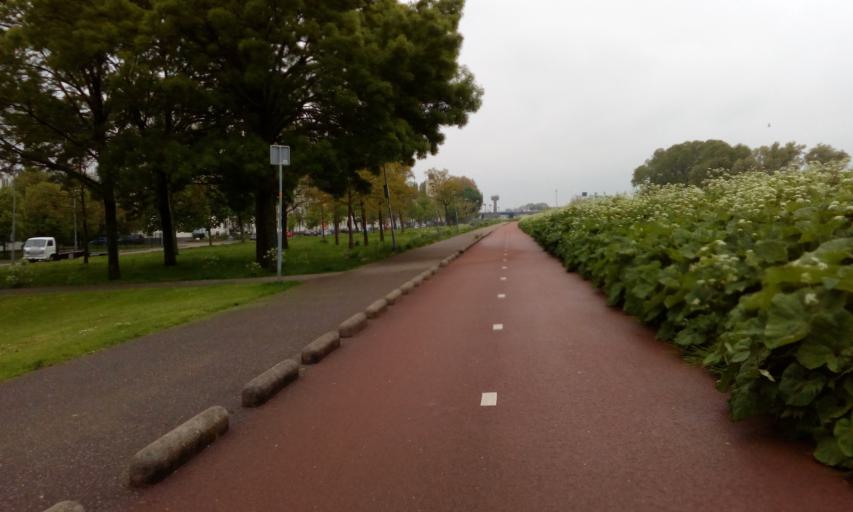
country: NL
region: South Holland
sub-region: Gemeente Schiedam
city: Schiedam
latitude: 51.9324
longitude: 4.4243
